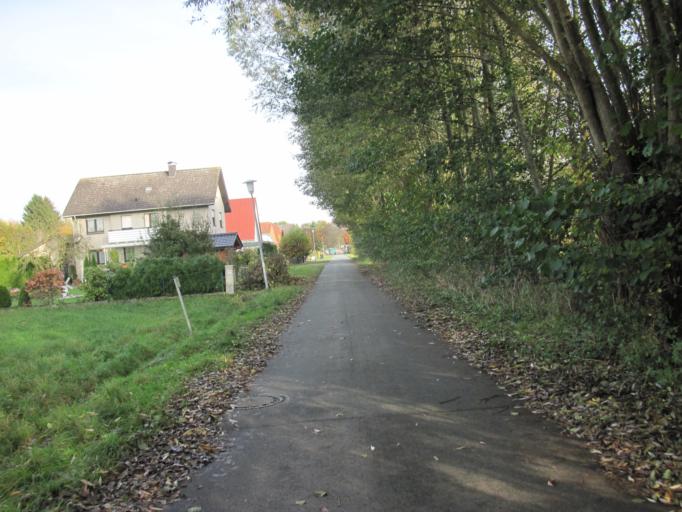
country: DE
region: North Rhine-Westphalia
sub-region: Regierungsbezirk Detmold
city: Hovelhof
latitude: 51.8052
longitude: 8.6682
